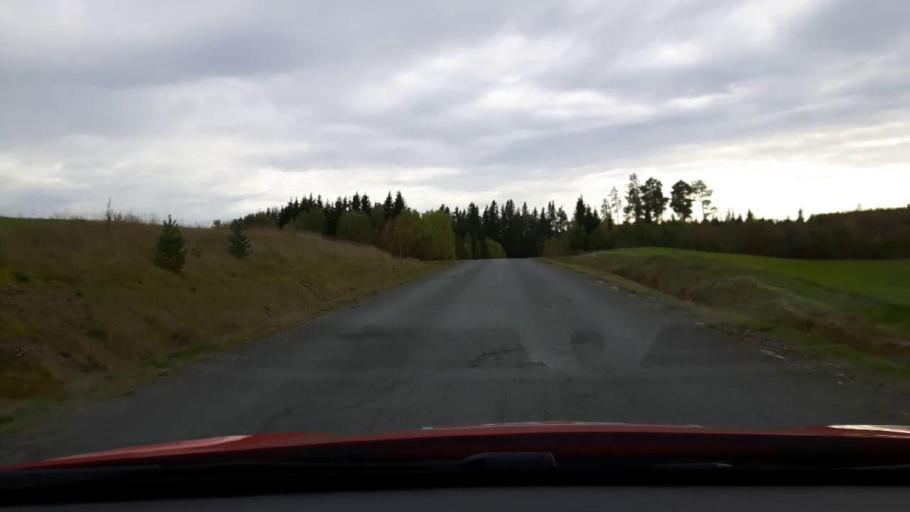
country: SE
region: Jaemtland
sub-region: Krokoms Kommun
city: Krokom
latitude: 63.2242
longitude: 14.1334
